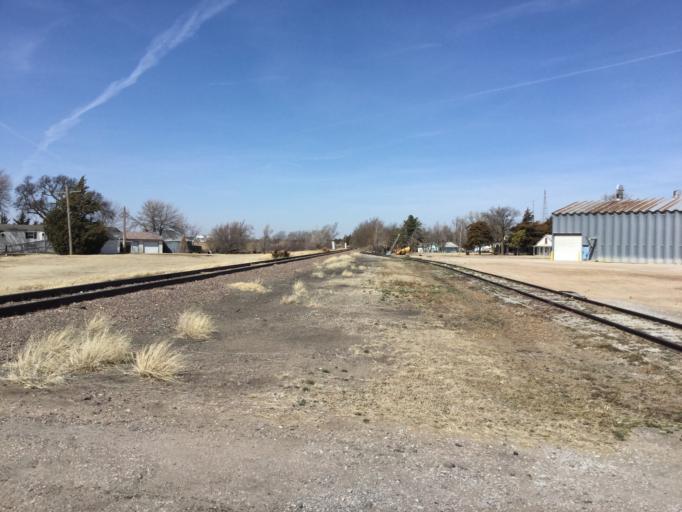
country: US
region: Kansas
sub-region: Rush County
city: La Crosse
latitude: 38.5333
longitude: -99.0541
